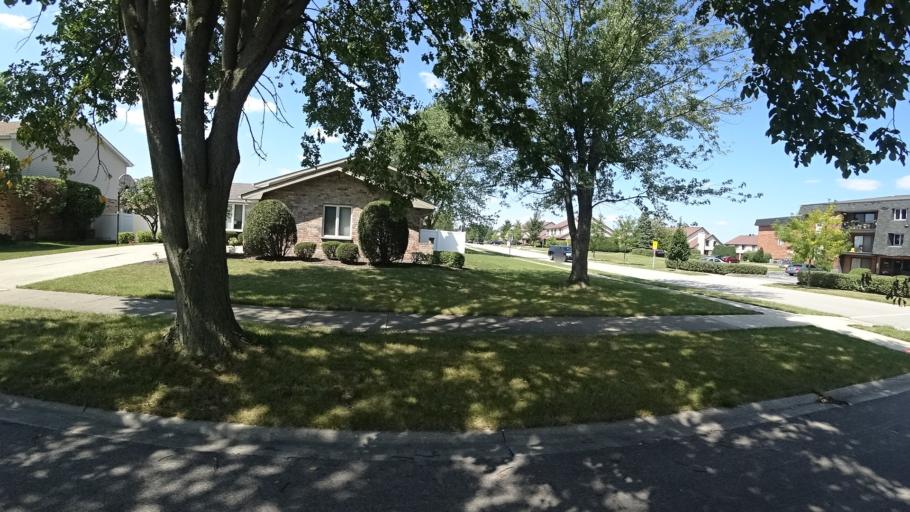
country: US
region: Illinois
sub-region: Cook County
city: Orland Park
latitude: 41.6362
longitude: -87.8446
